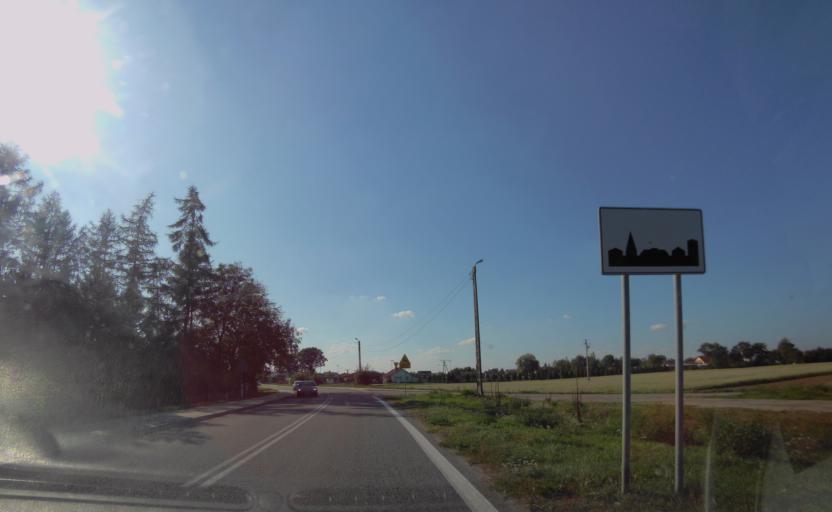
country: PL
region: Subcarpathian Voivodeship
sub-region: Powiat lezajski
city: Stare Miasto
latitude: 50.2918
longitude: 22.4373
